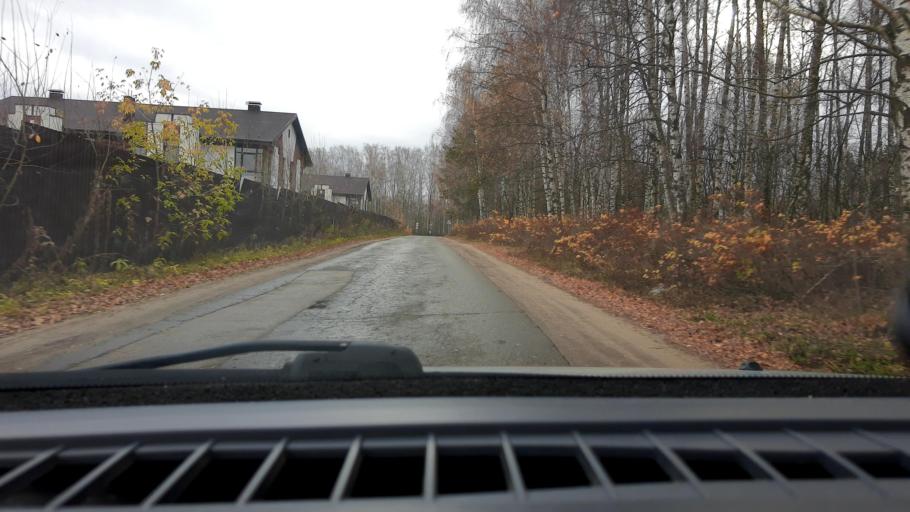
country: RU
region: Nizjnij Novgorod
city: Afonino
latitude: 56.1897
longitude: 44.1132
